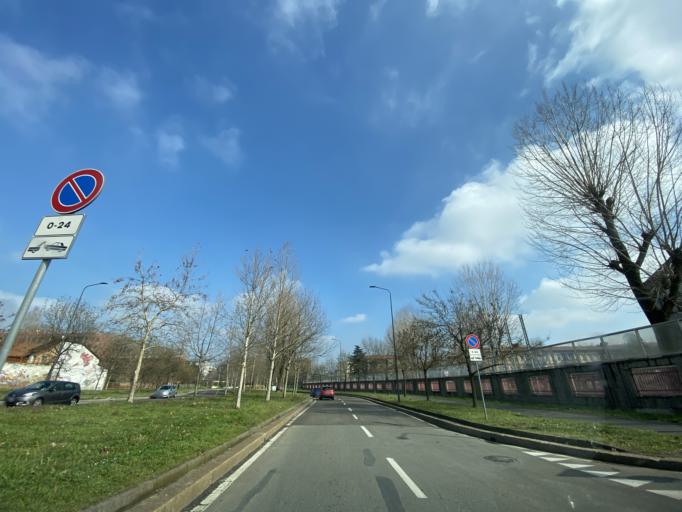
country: IT
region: Lombardy
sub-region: Citta metropolitana di Milano
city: Bresso
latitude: 45.5126
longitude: 9.1914
